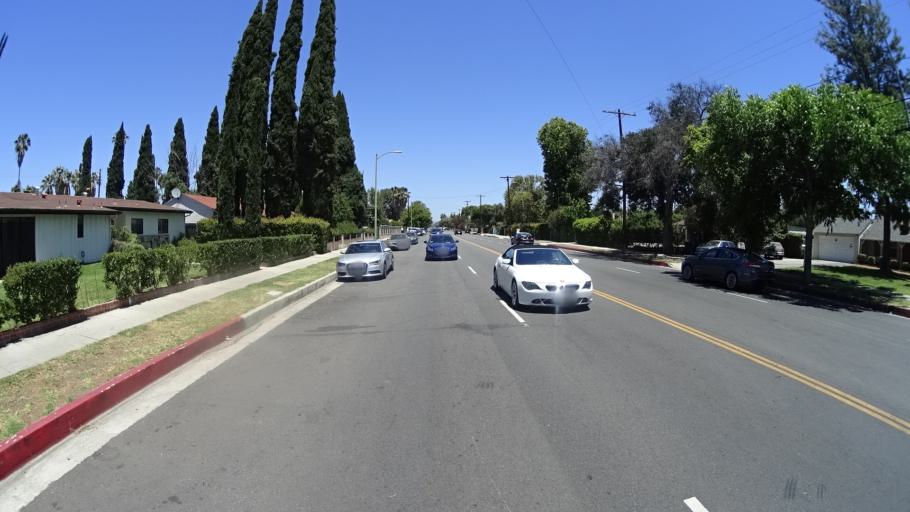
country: US
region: California
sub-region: Los Angeles County
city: Northridge
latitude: 34.1946
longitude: -118.5099
